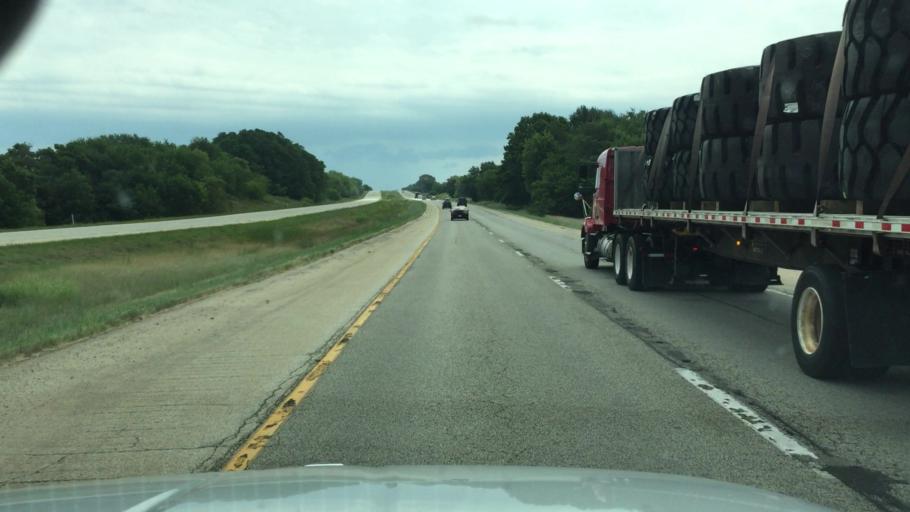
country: US
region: Illinois
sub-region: Peoria County
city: Elmwood
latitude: 40.8409
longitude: -89.9047
